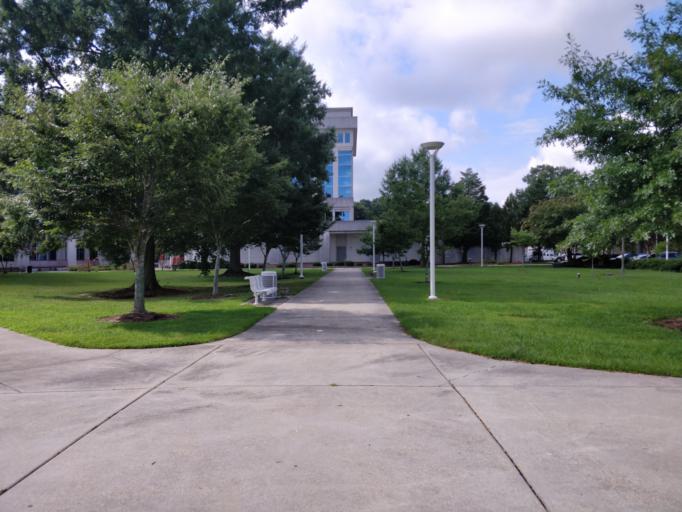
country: US
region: Virginia
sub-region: City of Chesapeake
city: Chesapeake
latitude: 36.7169
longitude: -76.2498
